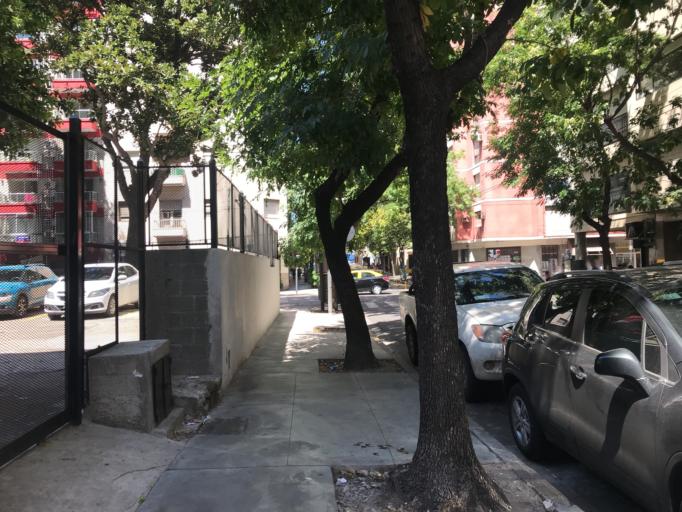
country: AR
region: Buenos Aires F.D.
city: Retiro
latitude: -34.6007
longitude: -58.3987
